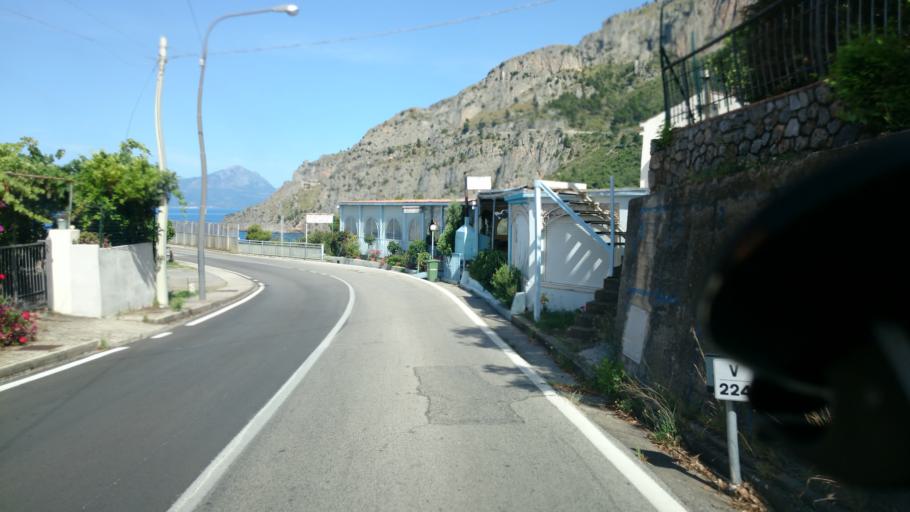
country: IT
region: Campania
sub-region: Provincia di Salerno
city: Sapri
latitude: 40.0362
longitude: 15.6717
